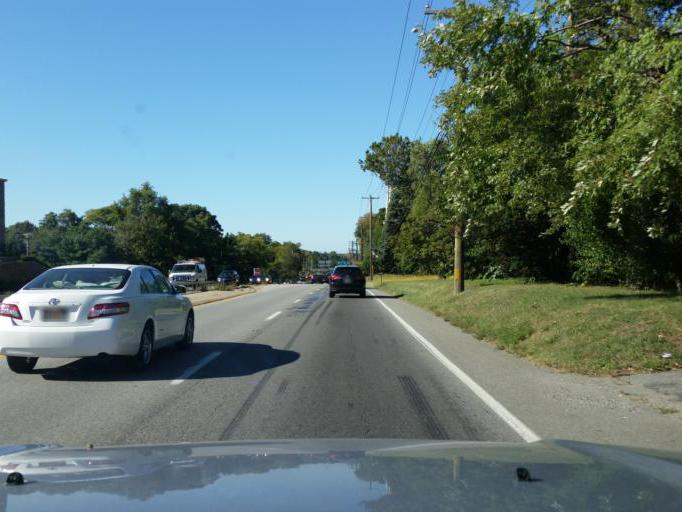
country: US
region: Pennsylvania
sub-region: Chester County
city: West Chester
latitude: 39.9341
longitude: -75.5880
